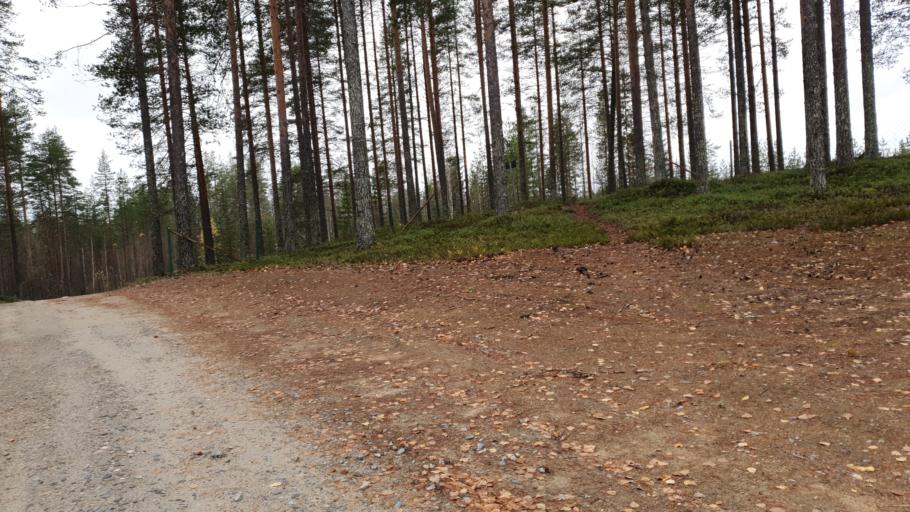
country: FI
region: Kainuu
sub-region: Kehys-Kainuu
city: Kuhmo
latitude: 64.1489
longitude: 29.4027
